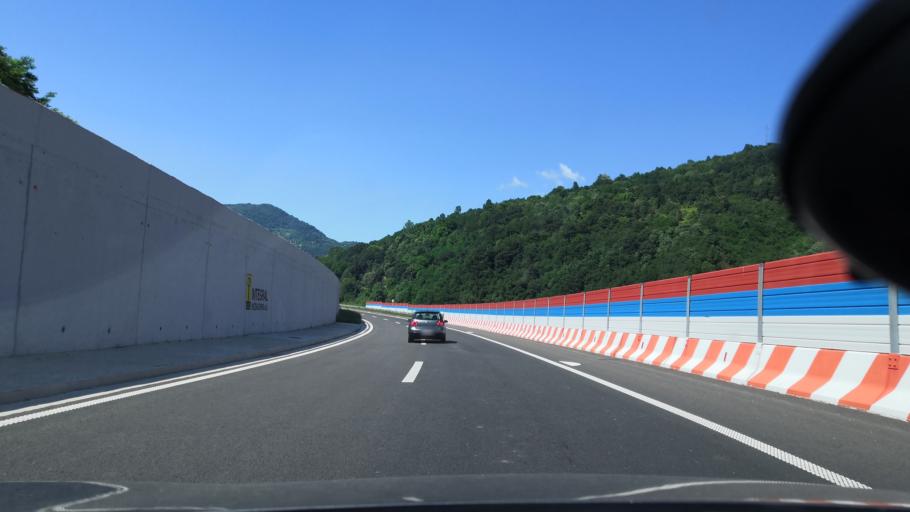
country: RS
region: Central Serbia
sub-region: Pcinjski Okrug
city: Vladicin Han
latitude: 42.7790
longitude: 22.0916
